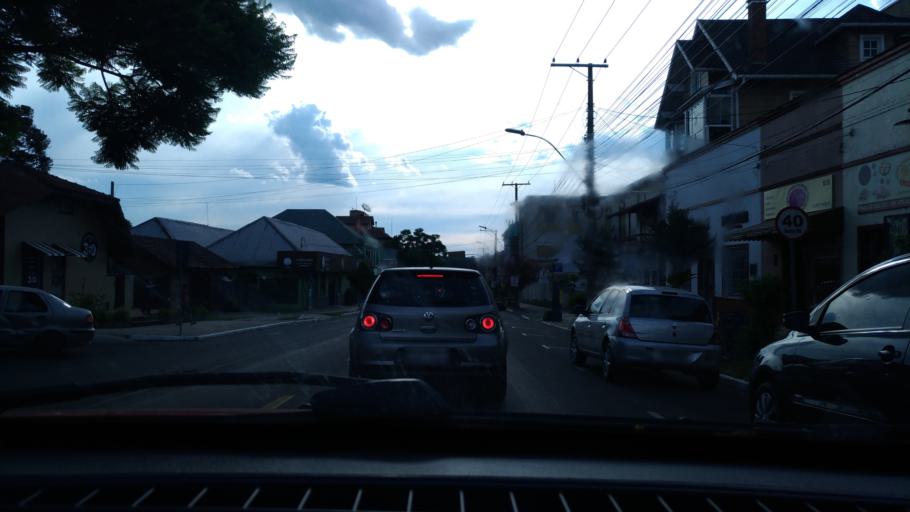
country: BR
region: Rio Grande do Sul
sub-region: Canela
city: Canela
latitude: -29.3627
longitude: -50.8116
